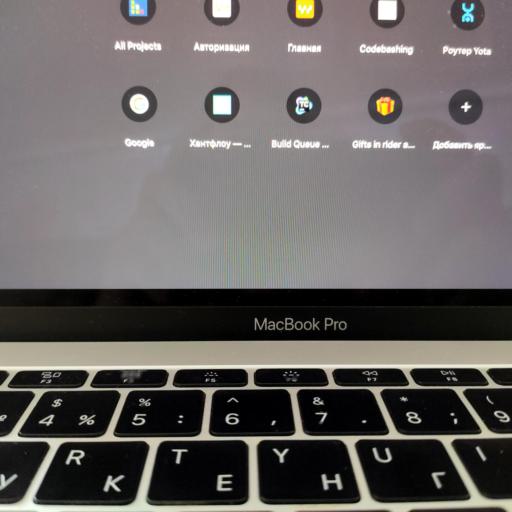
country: RU
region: Krasnodarskiy
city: Vysokoye
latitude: 43.4875
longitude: 39.9910
